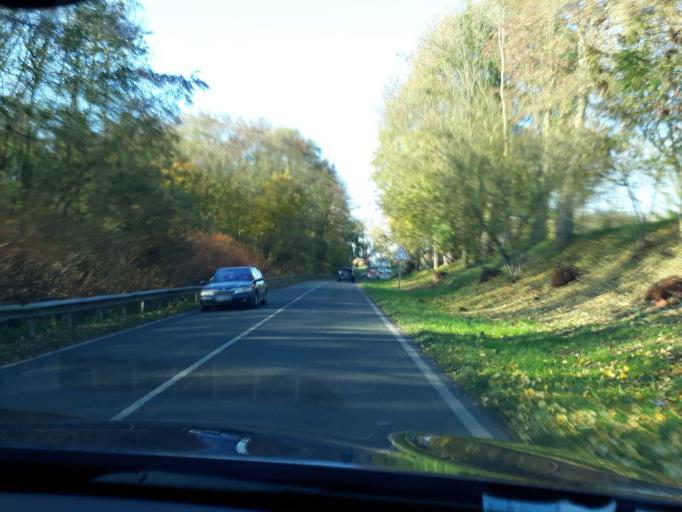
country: FR
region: Nord-Pas-de-Calais
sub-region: Departement du Nord
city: Sin-le-Noble
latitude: 50.3618
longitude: 3.1274
